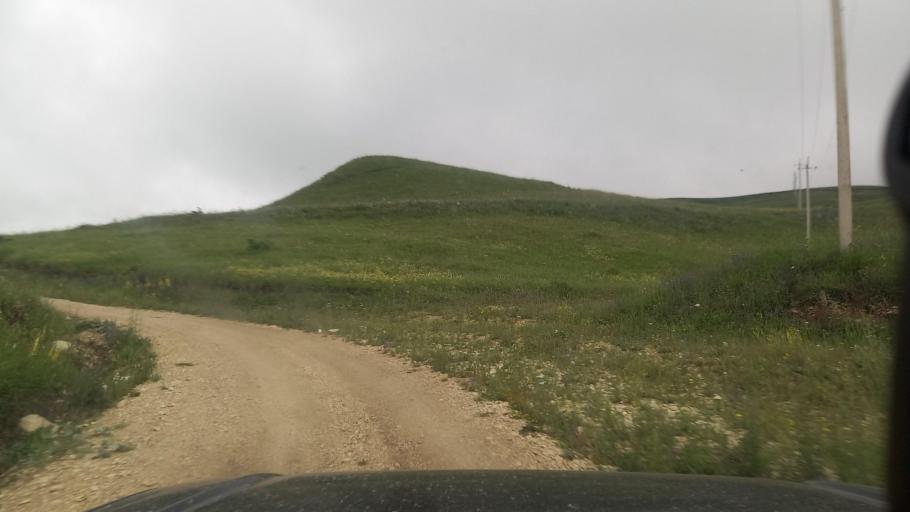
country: RU
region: Karachayevo-Cherkesiya
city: Pregradnaya
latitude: 44.0084
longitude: 41.1691
